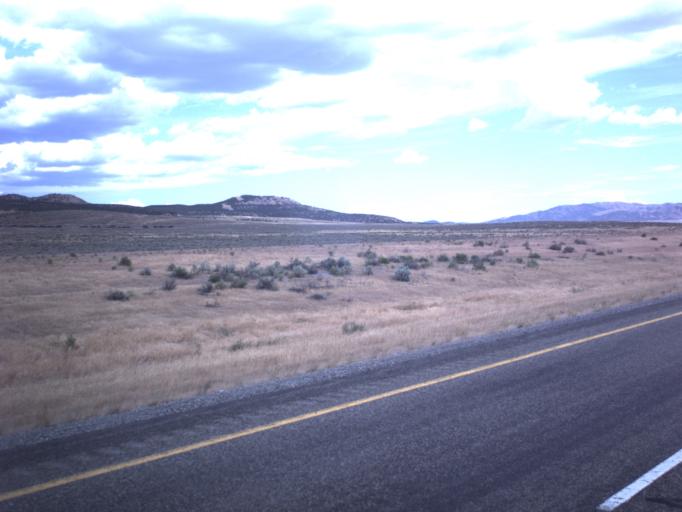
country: US
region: Idaho
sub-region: Oneida County
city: Malad City
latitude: 41.9965
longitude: -112.8306
